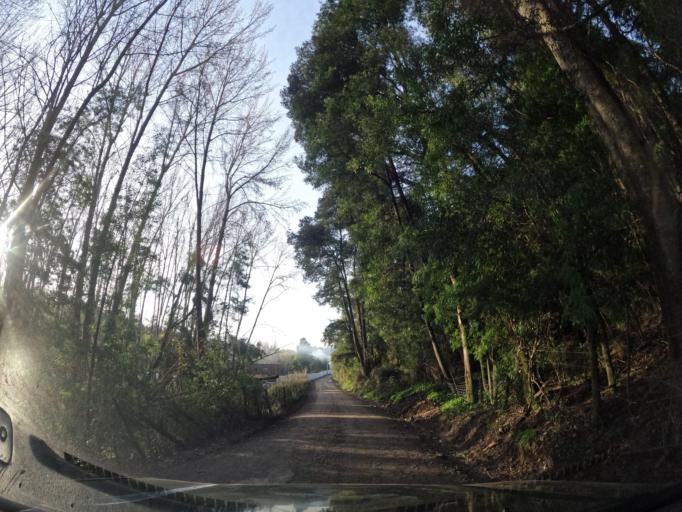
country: CL
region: Biobio
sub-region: Provincia de Concepcion
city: Concepcion
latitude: -36.8654
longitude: -72.9988
